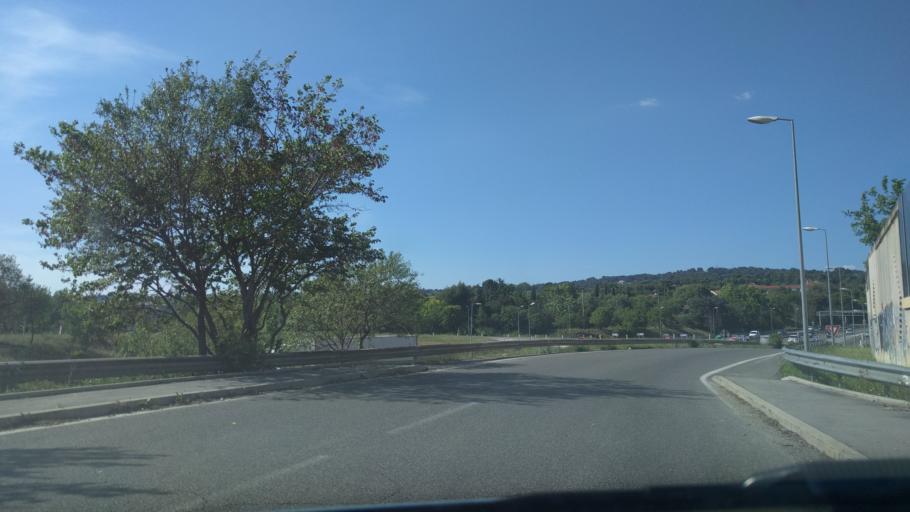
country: FR
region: Provence-Alpes-Cote d'Azur
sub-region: Departement des Bouches-du-Rhone
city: Aix-en-Provence
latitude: 43.5285
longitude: 5.4282
